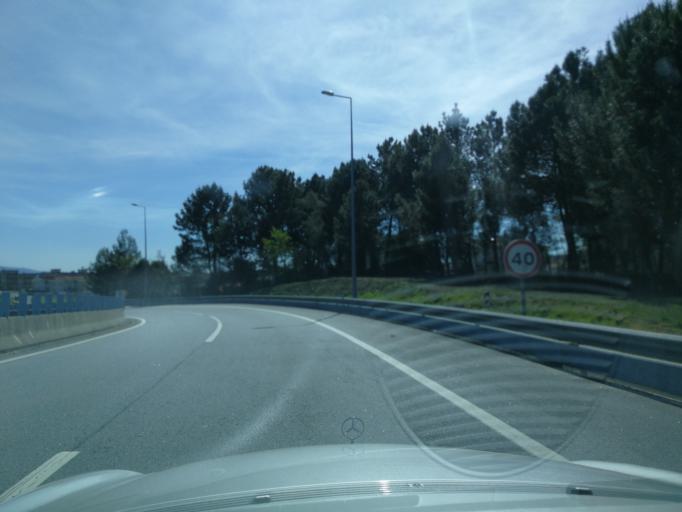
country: PT
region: Braga
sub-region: Vila Nova de Famalicao
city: Calendario
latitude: 41.3853
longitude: -8.5177
